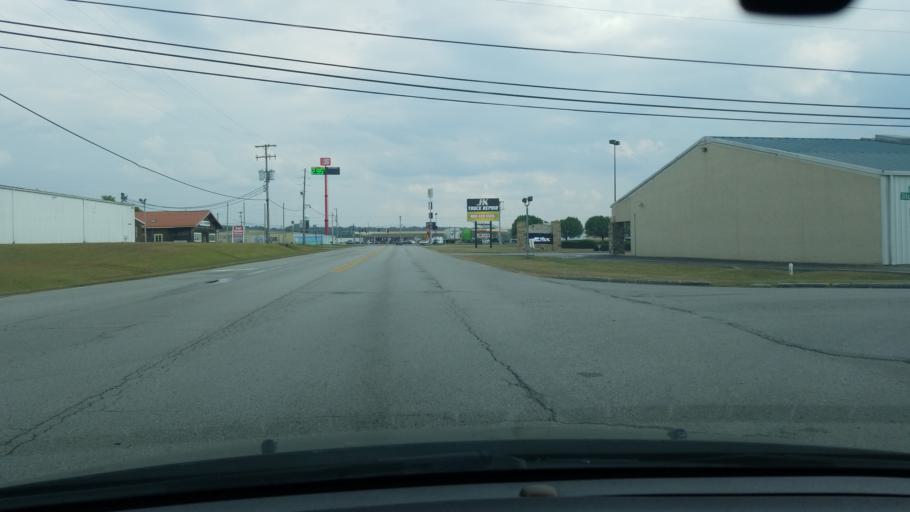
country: US
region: Tennessee
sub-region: Cumberland County
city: Crossville
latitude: 35.9798
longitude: -85.0175
